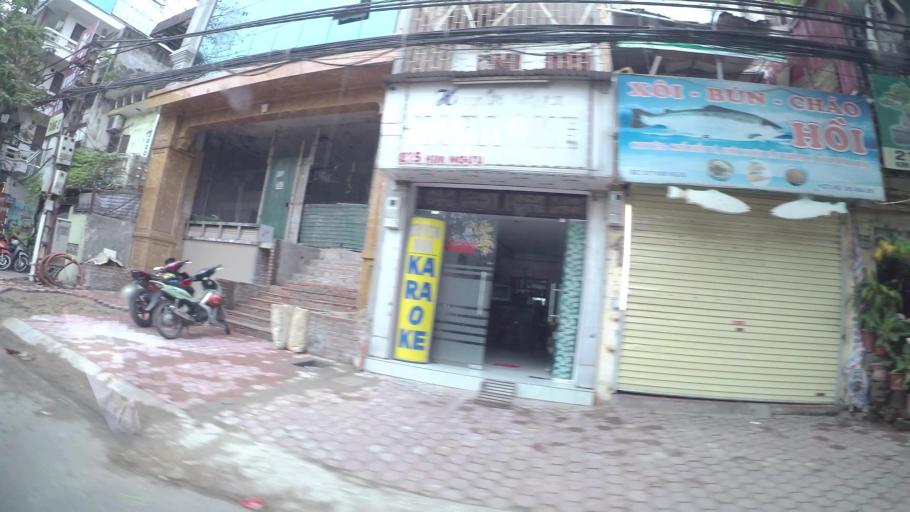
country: VN
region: Ha Noi
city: Hai BaTrung
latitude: 21.0052
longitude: 105.8616
